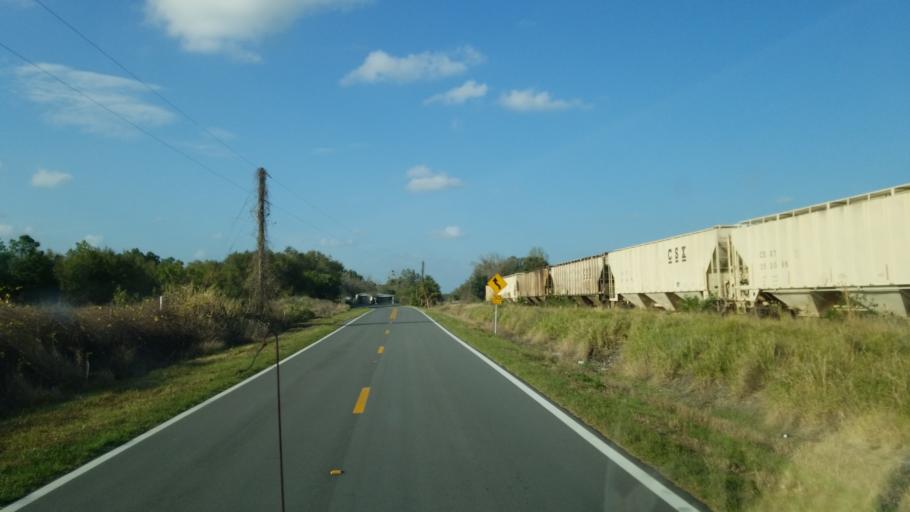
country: US
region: Florida
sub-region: Polk County
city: Mulberry
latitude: 27.7891
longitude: -81.9777
